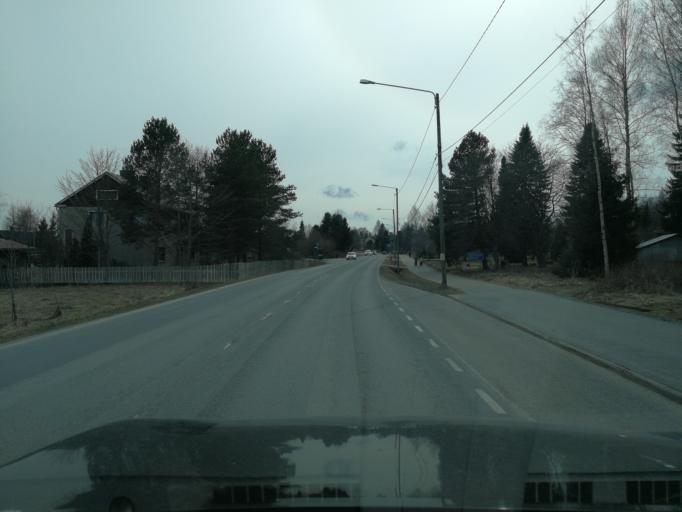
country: FI
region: Uusimaa
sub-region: Helsinki
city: Lohja
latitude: 60.2023
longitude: 24.0074
